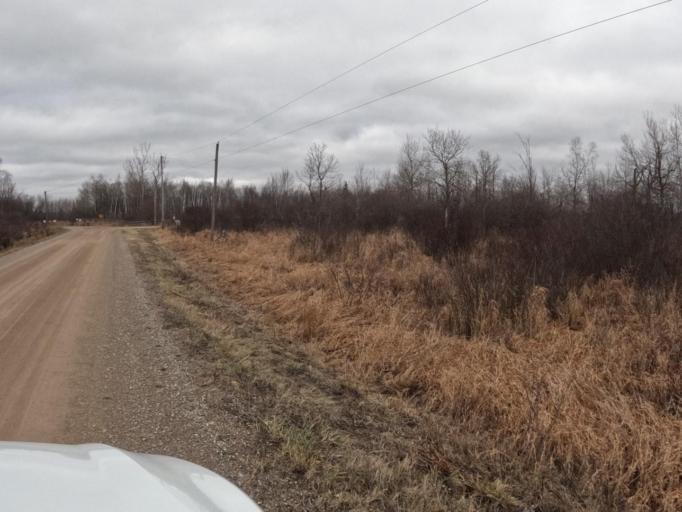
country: CA
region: Ontario
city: Shelburne
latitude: 43.8970
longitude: -80.3845
